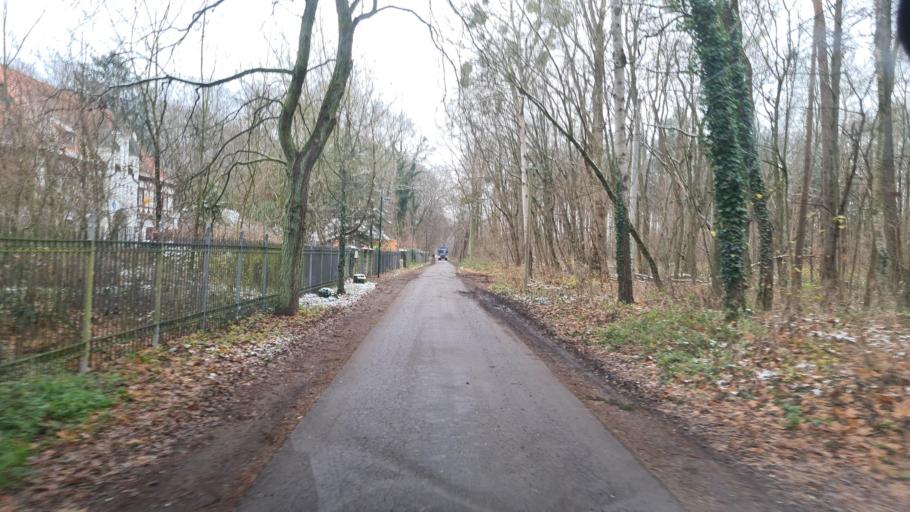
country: DE
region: Brandenburg
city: Rehfelde
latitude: 52.4560
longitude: 13.9182
